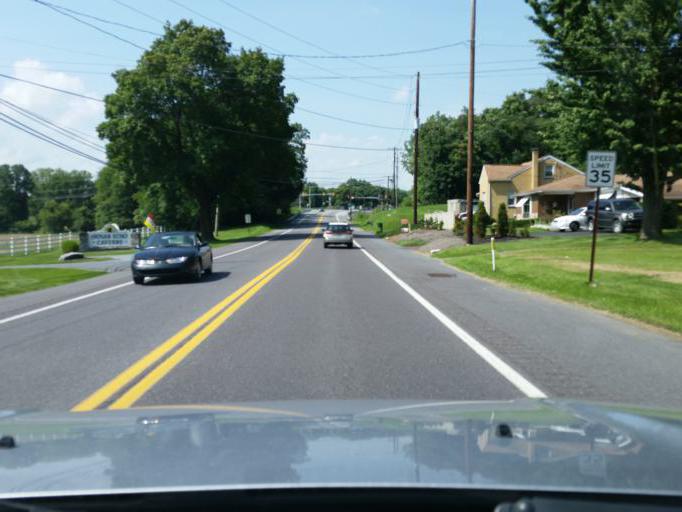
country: US
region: Pennsylvania
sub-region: Dauphin County
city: Hummelstown
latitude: 40.2552
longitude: -76.7089
